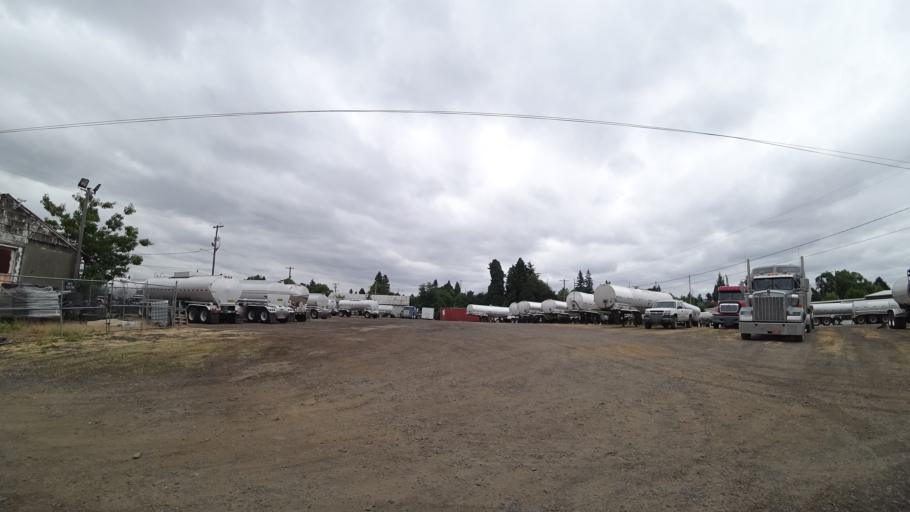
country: US
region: Washington
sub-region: Clark County
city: Vancouver
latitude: 45.5901
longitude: -122.6957
